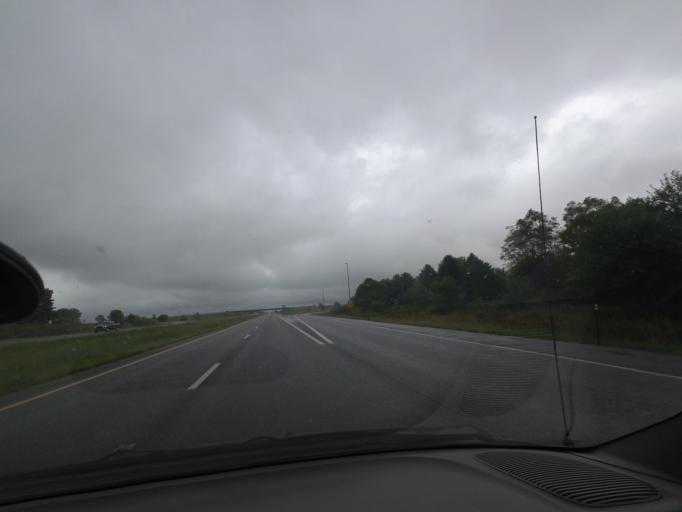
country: US
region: Illinois
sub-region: Champaign County
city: Mahomet
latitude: 40.1203
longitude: -88.4127
